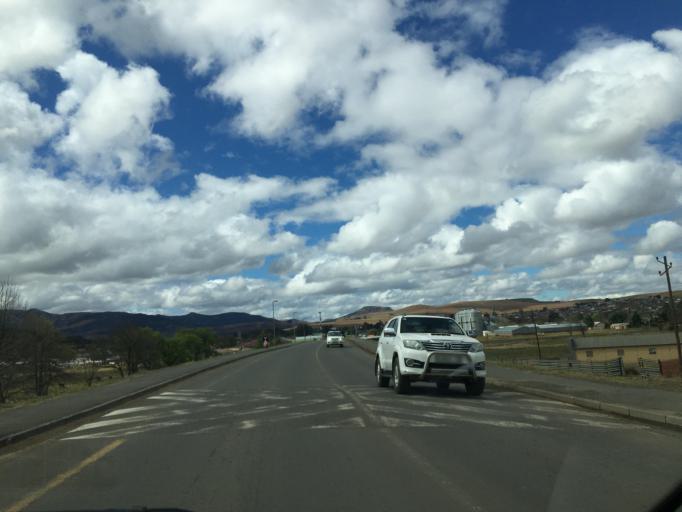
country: ZA
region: Eastern Cape
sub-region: Chris Hani District Municipality
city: Elliot
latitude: -31.3368
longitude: 27.8409
